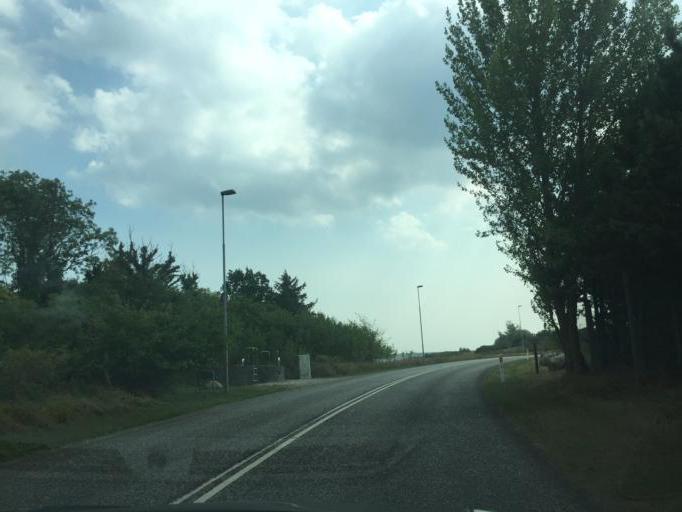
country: DK
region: South Denmark
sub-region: Nyborg Kommune
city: Nyborg
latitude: 55.3012
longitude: 10.8178
